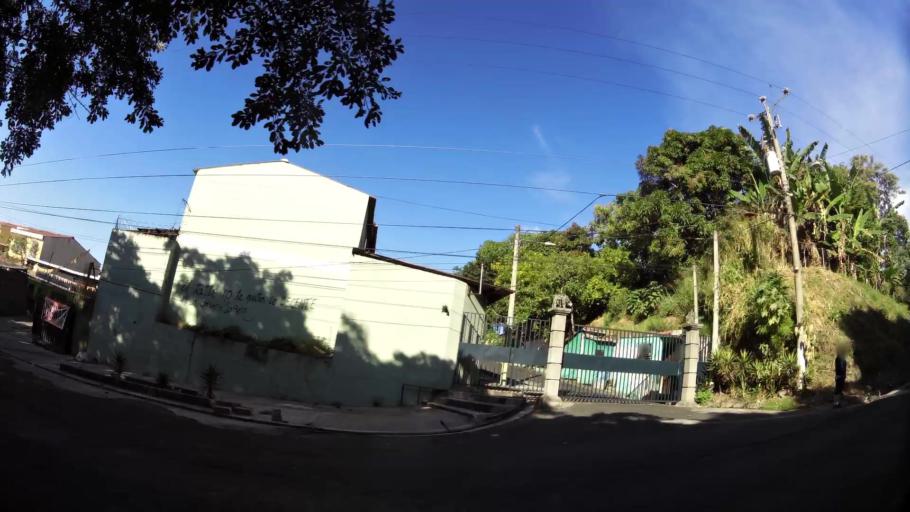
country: SV
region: La Libertad
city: Santa Tecla
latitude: 13.6865
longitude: -89.2877
